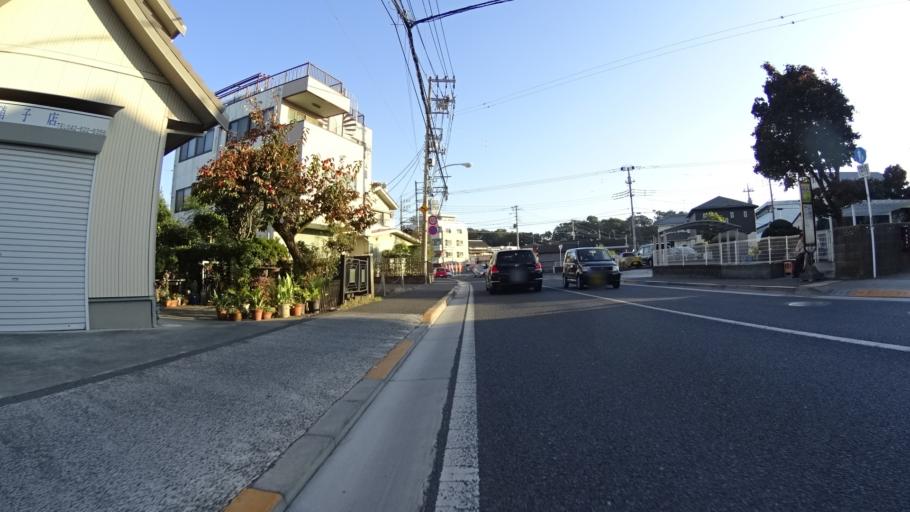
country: JP
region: Tokyo
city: Hachioji
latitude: 35.6668
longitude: 139.3028
